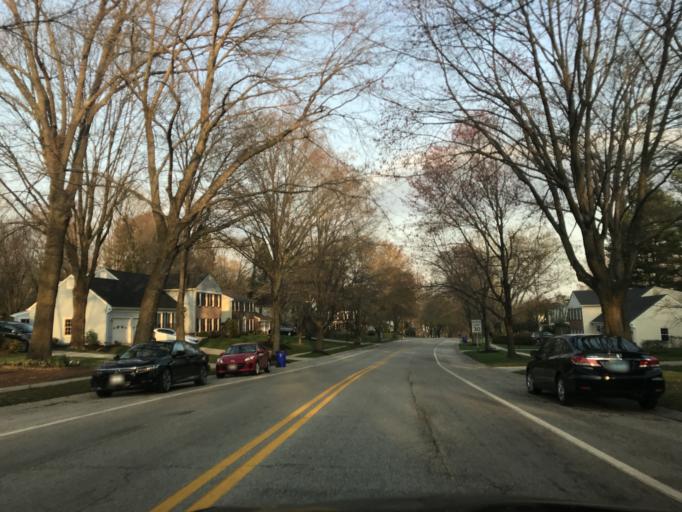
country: US
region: Maryland
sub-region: Howard County
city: Columbia
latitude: 39.2341
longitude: -76.8565
